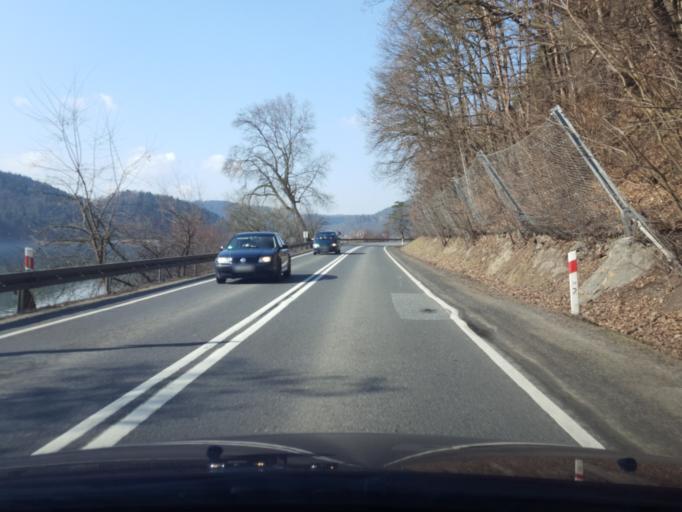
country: PL
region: Lesser Poland Voivodeship
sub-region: Powiat brzeski
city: Czchow
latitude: 49.8102
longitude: 20.6726
